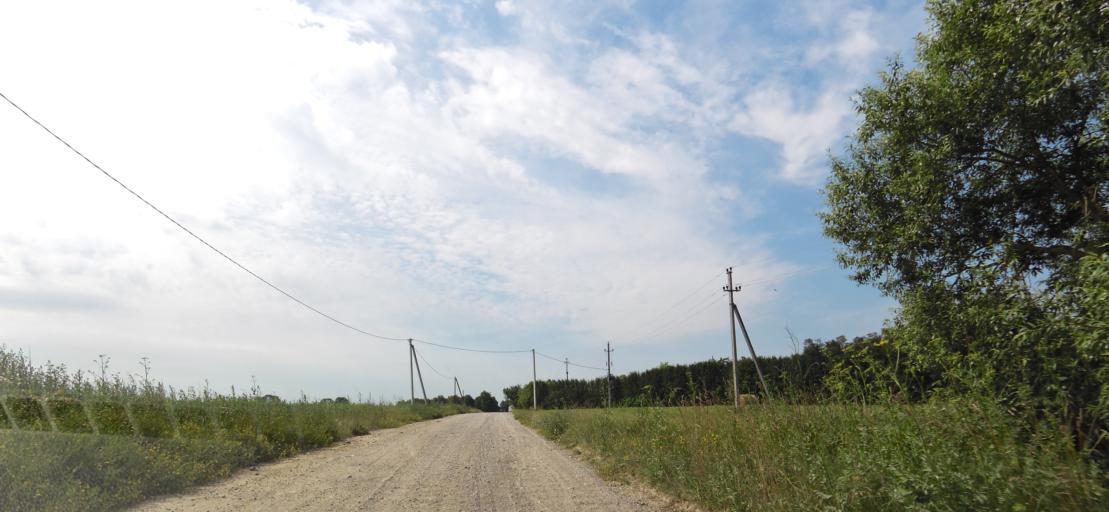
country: LT
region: Panevezys
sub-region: Birzai
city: Birzai
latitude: 56.2113
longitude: 24.6667
